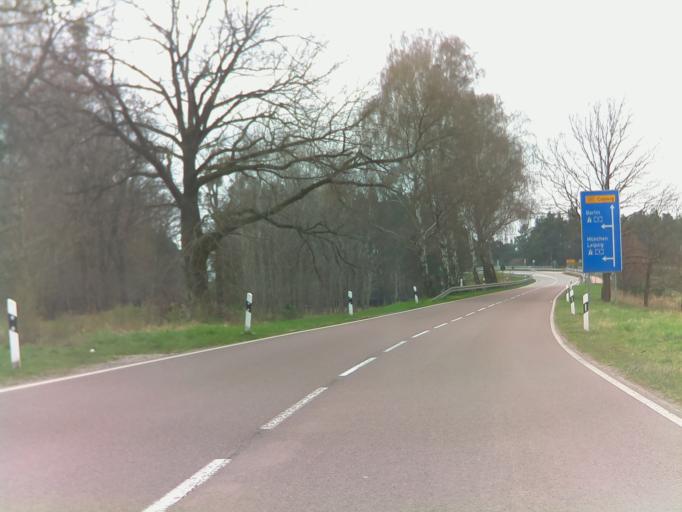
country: DE
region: Saxony-Anhalt
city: Coswig
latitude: 51.9661
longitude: 12.4653
